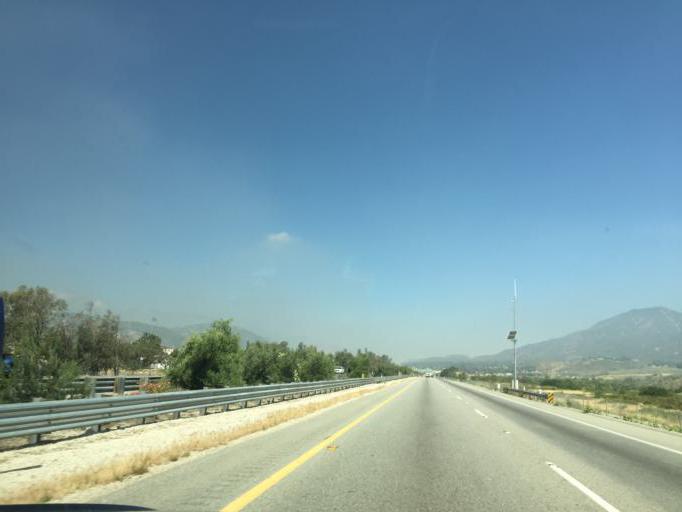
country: US
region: California
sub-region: San Bernardino County
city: Muscoy
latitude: 34.2065
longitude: -117.3813
